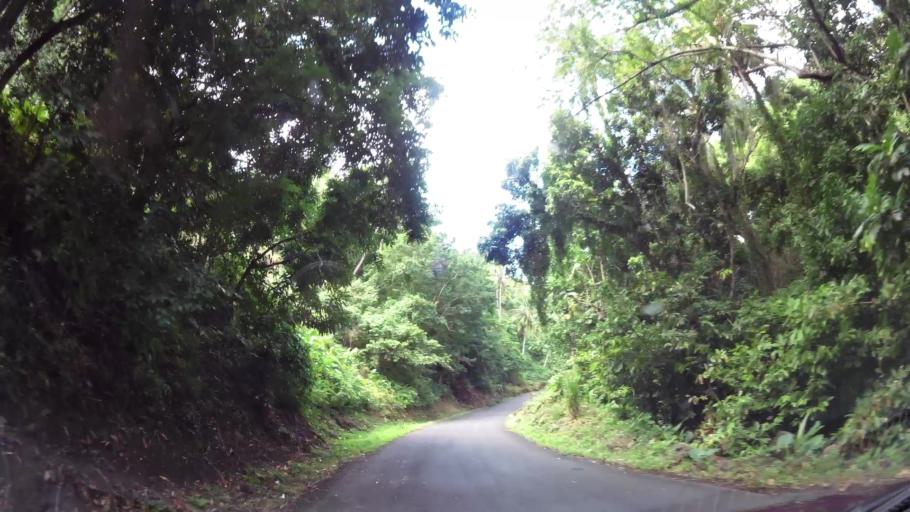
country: DM
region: Saint John
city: Portsmouth
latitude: 15.6249
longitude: -61.4625
